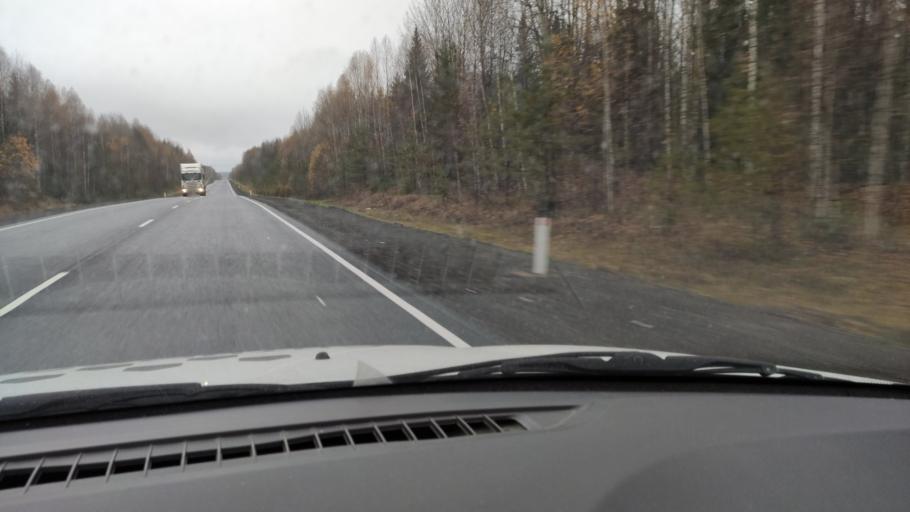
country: RU
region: Kirov
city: Chernaya Kholunitsa
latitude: 58.8821
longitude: 51.4269
